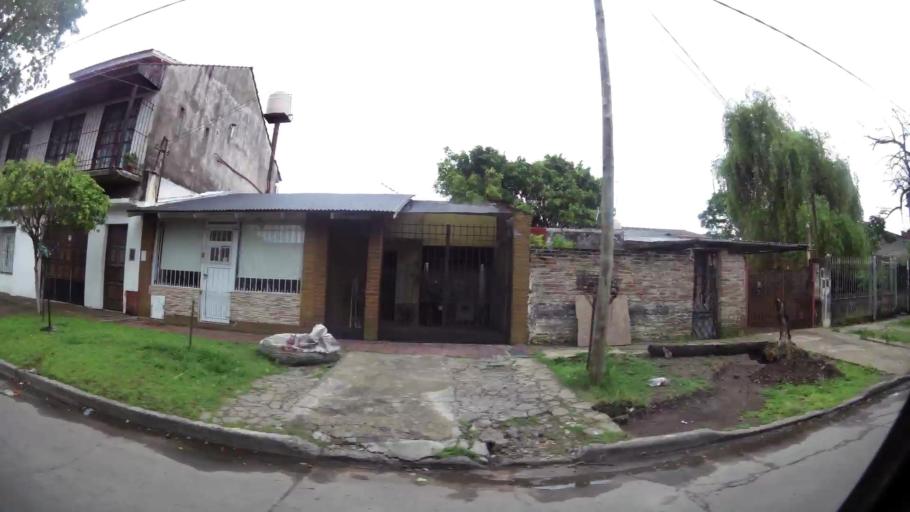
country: AR
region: Buenos Aires
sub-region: Partido de Lomas de Zamora
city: Lomas de Zamora
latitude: -34.7508
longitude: -58.3687
